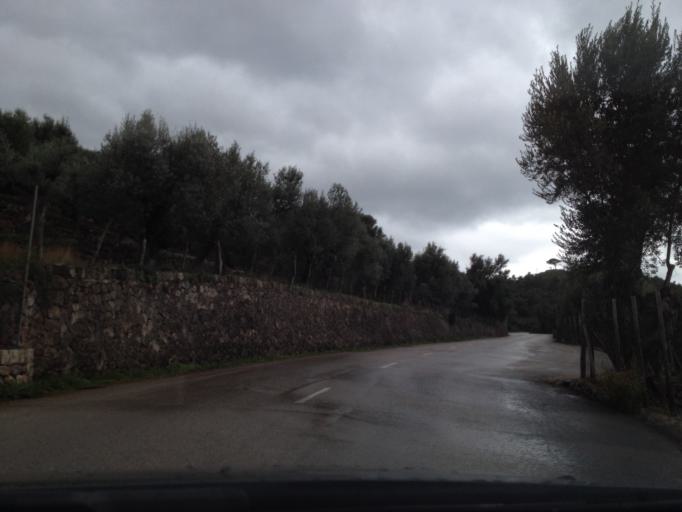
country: ES
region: Balearic Islands
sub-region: Illes Balears
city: Soller
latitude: 39.7736
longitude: 2.6834
